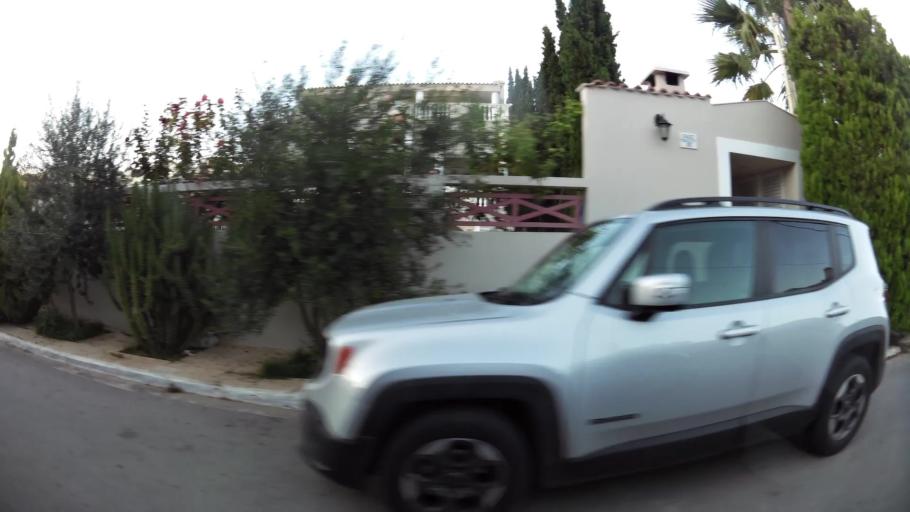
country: GR
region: Attica
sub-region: Nomarchia Anatolikis Attikis
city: Vari
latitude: 37.8222
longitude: 23.7967
